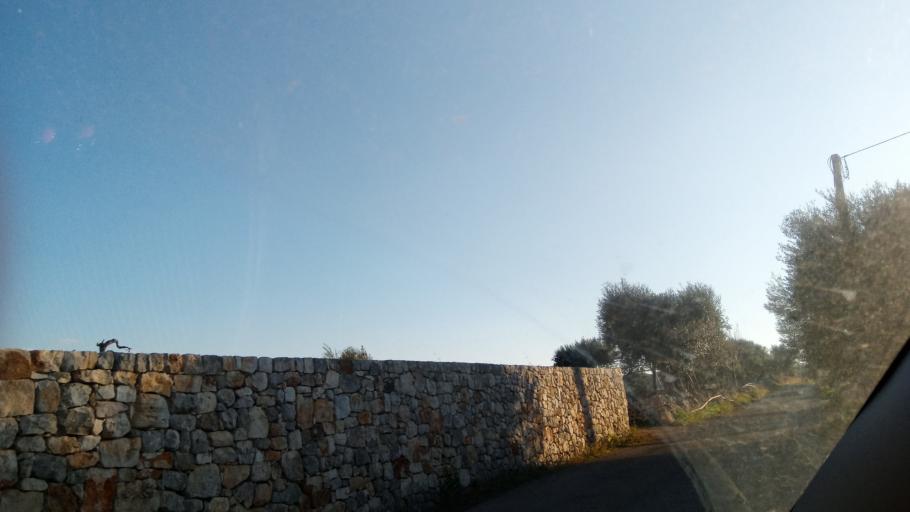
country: IT
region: Apulia
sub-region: Provincia di Bari
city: Polignano a Mare
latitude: 40.9801
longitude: 17.2084
